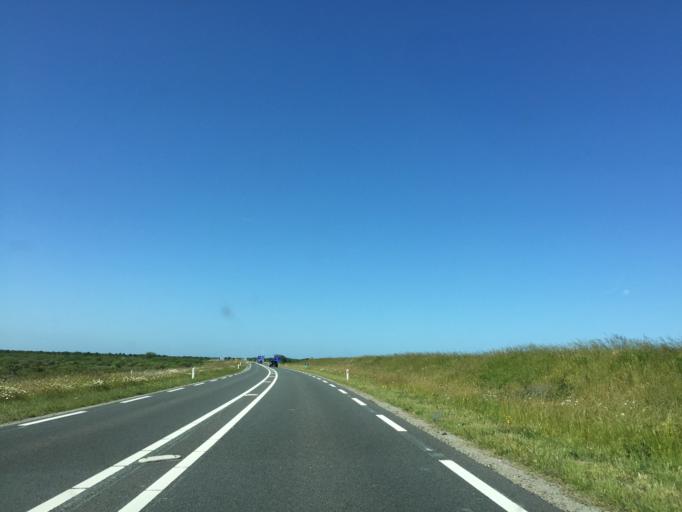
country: NL
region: South Holland
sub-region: Gemeente Goeree-Overflakkee
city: Ouddorp
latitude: 51.7954
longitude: 3.8932
